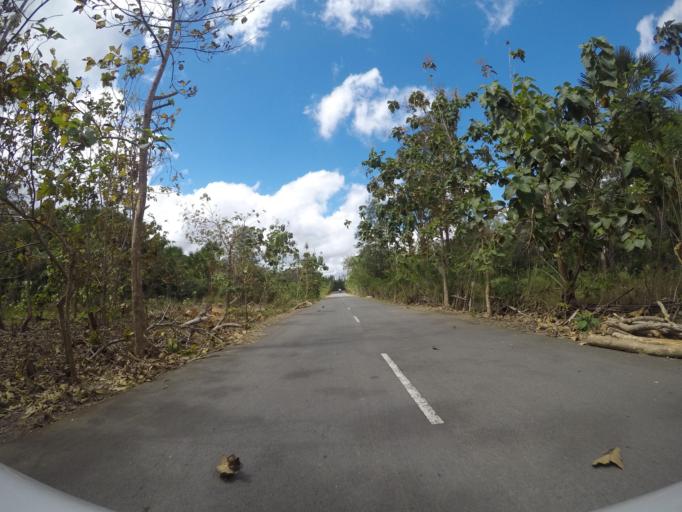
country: TL
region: Lautem
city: Lospalos
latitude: -8.4643
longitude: 126.8208
